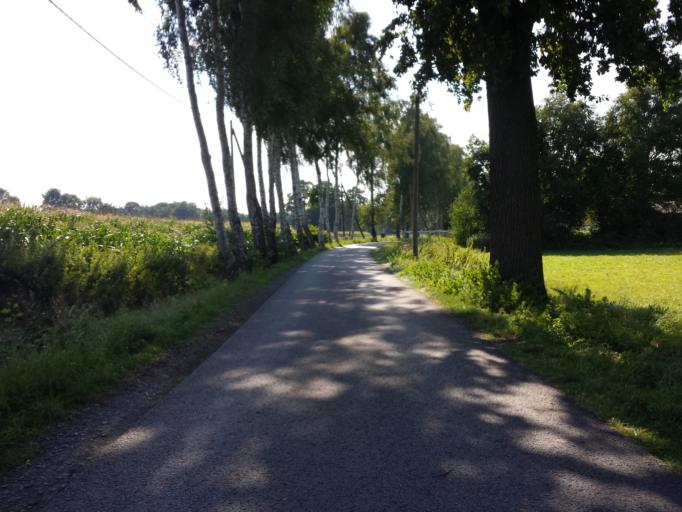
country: DE
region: North Rhine-Westphalia
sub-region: Regierungsbezirk Detmold
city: Guetersloh
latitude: 51.8780
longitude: 8.3731
